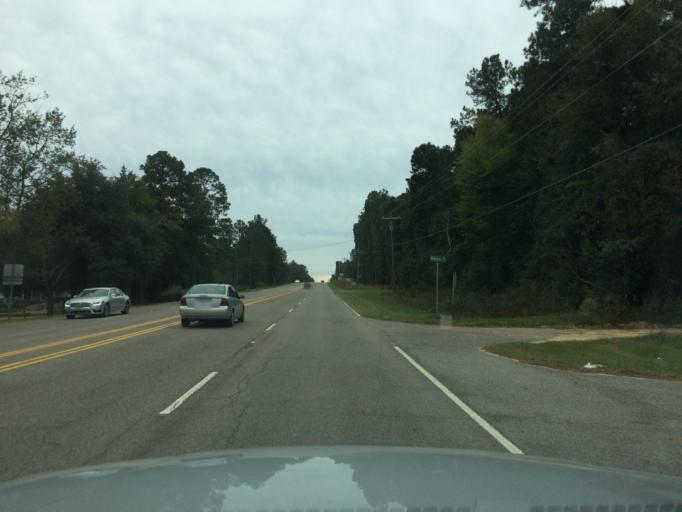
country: US
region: South Carolina
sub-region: Aiken County
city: New Ellenton
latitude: 33.4443
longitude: -81.6866
